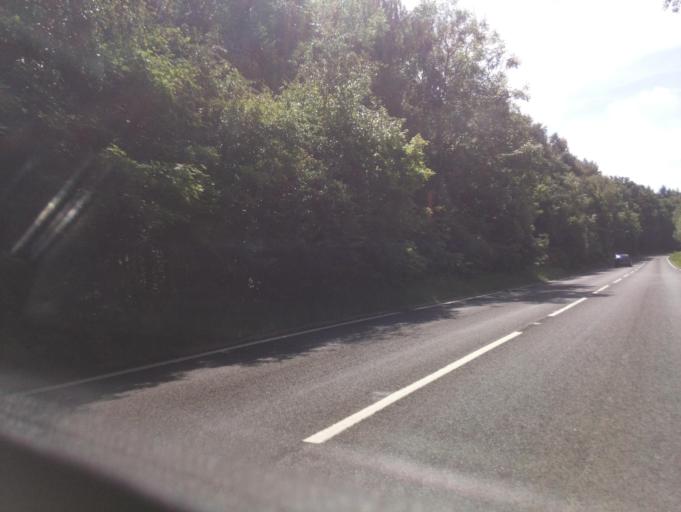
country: GB
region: England
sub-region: North Lincolnshire
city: Broughton
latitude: 53.5458
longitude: -0.5774
